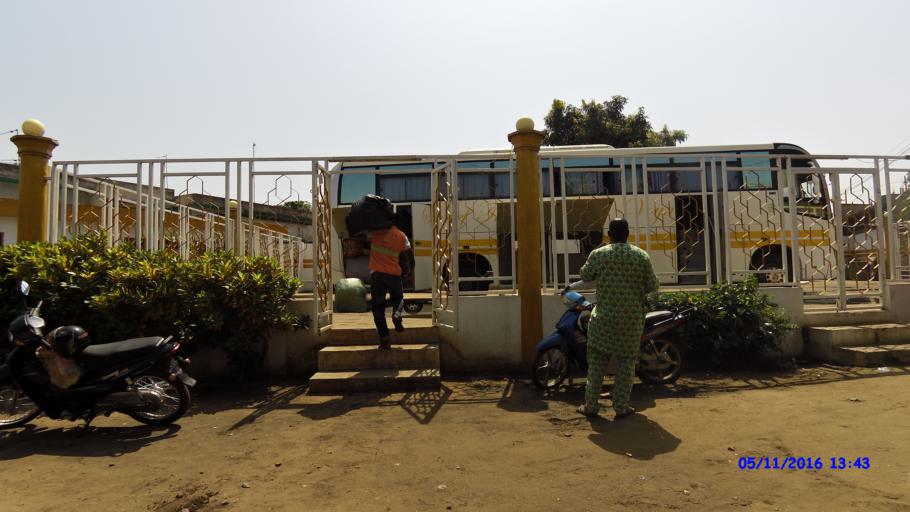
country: BJ
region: Littoral
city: Cotonou
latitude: 6.3582
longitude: 2.4201
